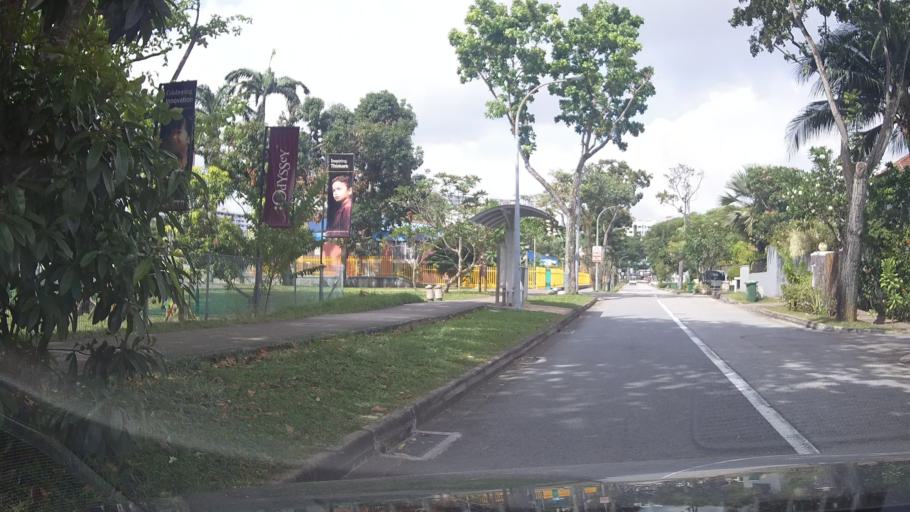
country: SG
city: Singapore
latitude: 1.3026
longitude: 103.8876
